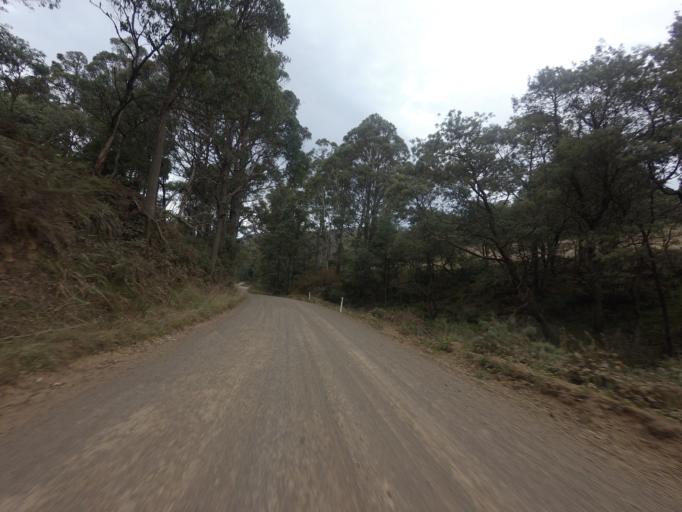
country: AU
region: Tasmania
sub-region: Derwent Valley
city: New Norfolk
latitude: -42.5811
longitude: 147.0069
